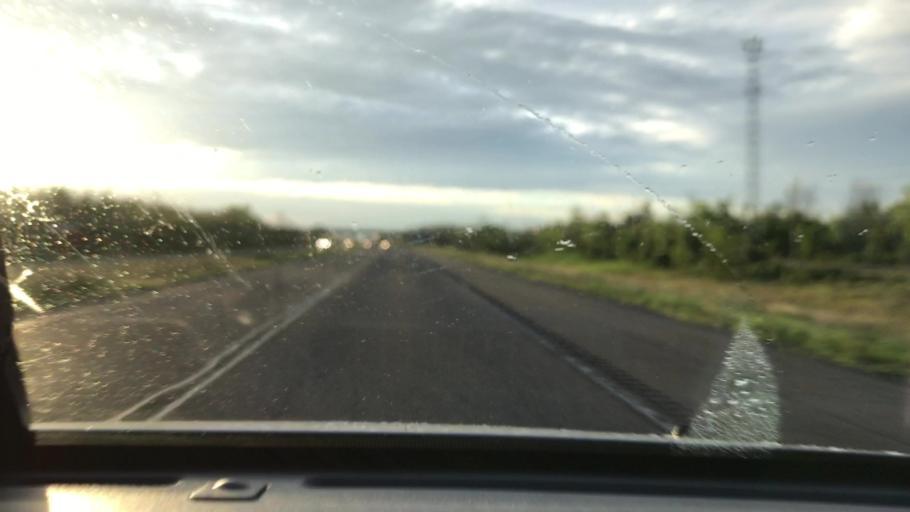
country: US
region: New York
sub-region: Erie County
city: Grandyle Village
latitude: 42.9489
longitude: -79.0024
